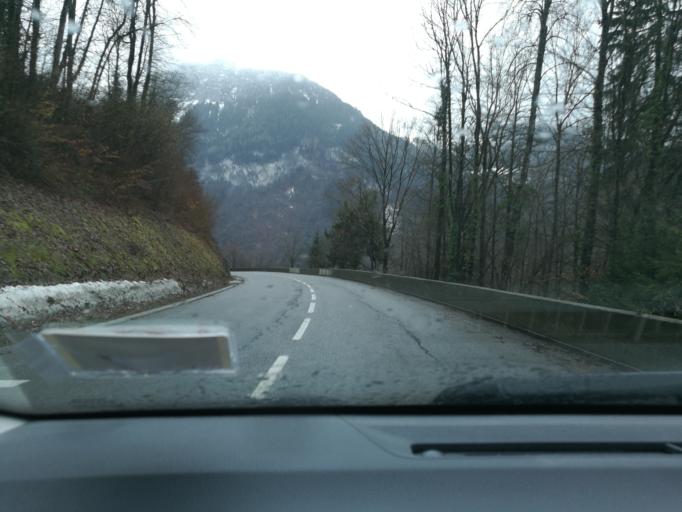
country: FR
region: Rhone-Alpes
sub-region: Departement de la Haute-Savoie
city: Araches-la-Frasse
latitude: 46.0479
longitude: 6.6156
